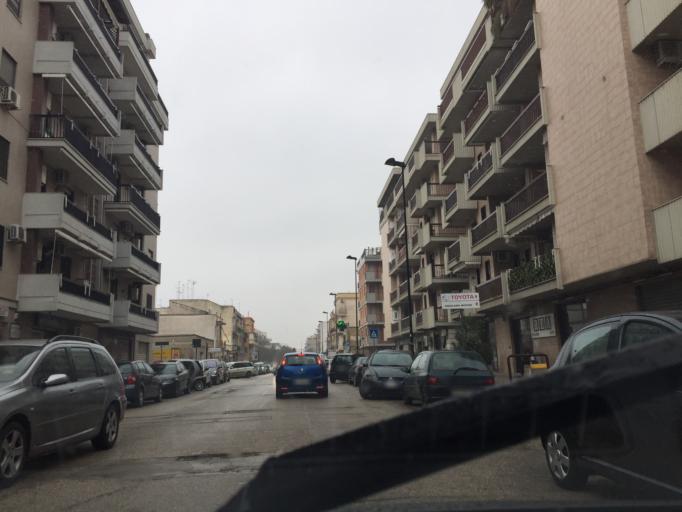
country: IT
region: Apulia
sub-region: Provincia di Foggia
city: Foggia
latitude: 41.4666
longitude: 15.5318
